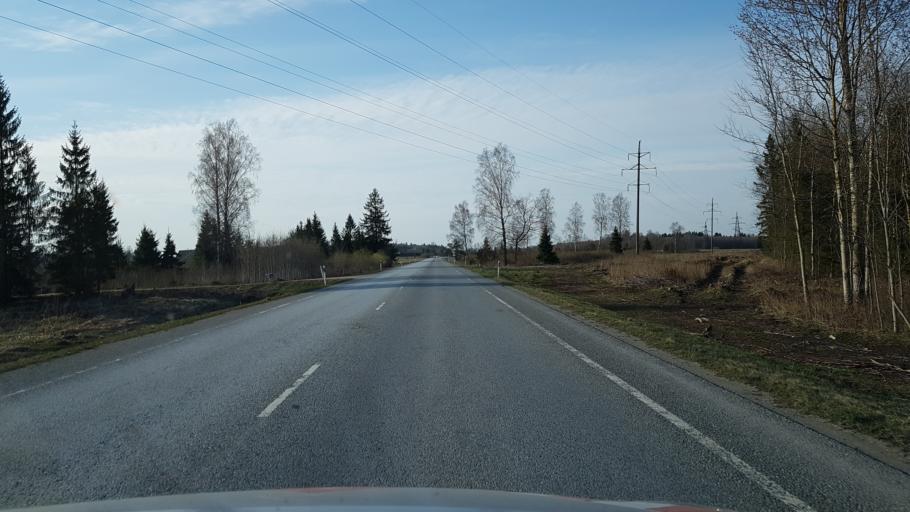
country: EE
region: Laeaene-Virumaa
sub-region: Rakvere linn
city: Rakvere
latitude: 59.3864
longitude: 26.3161
